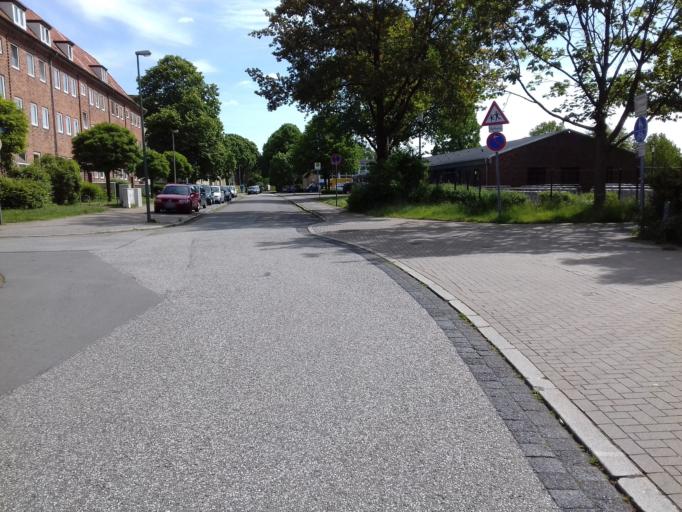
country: DE
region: Schleswig-Holstein
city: Neumunster
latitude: 54.0816
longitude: 9.9958
